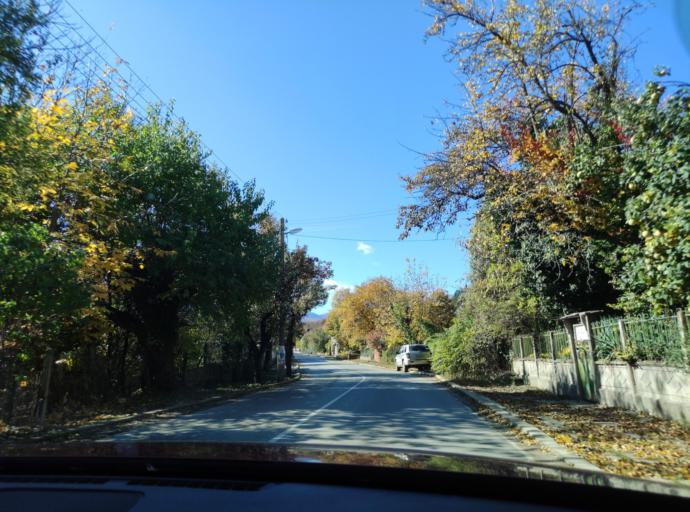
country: BG
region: Montana
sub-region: Obshtina Chiprovtsi
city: Chiprovtsi
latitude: 43.4343
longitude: 22.9699
